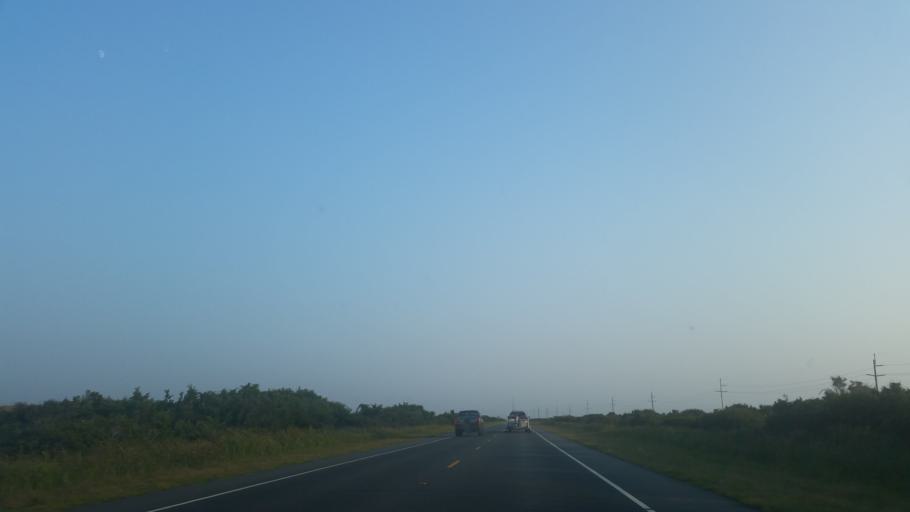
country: US
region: North Carolina
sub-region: Dare County
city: Wanchese
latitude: 35.6373
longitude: -75.4727
